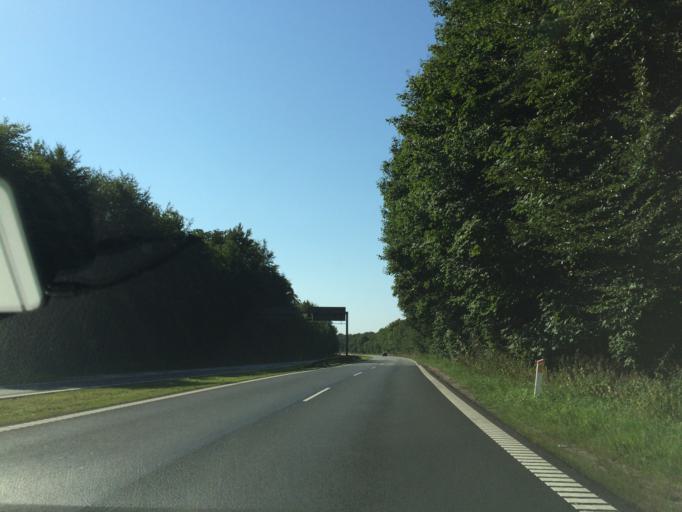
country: DK
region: South Denmark
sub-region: Kolding Kommune
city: Kolding
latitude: 55.5301
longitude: 9.4963
